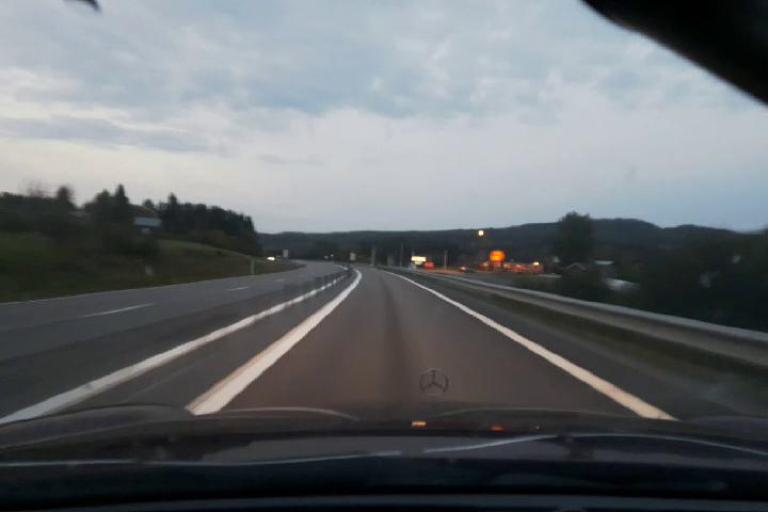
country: SE
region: Vaesternorrland
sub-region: Kramfors Kommun
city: Nordingra
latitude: 62.9694
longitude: 18.1593
